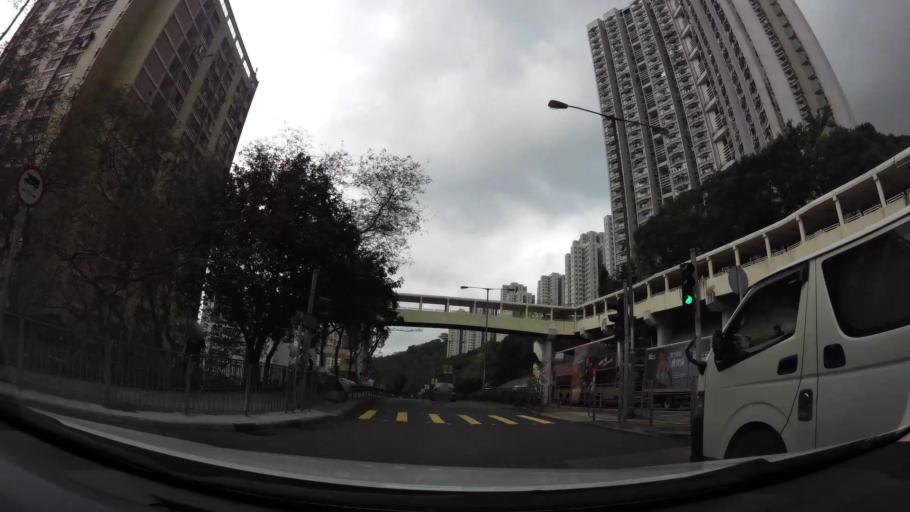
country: HK
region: Wong Tai Sin
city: Wong Tai Sin
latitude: 22.3450
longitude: 114.1911
